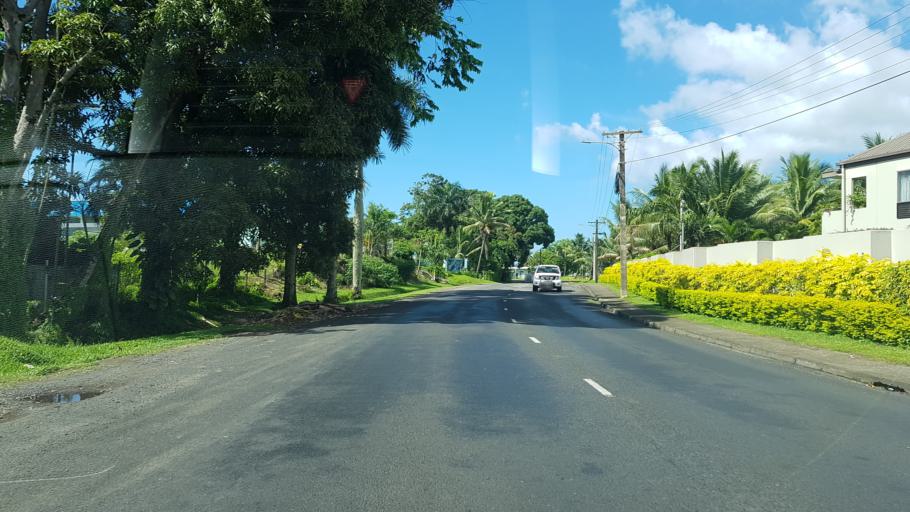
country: FJ
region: Central
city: Suva
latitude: -18.1468
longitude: 178.4537
